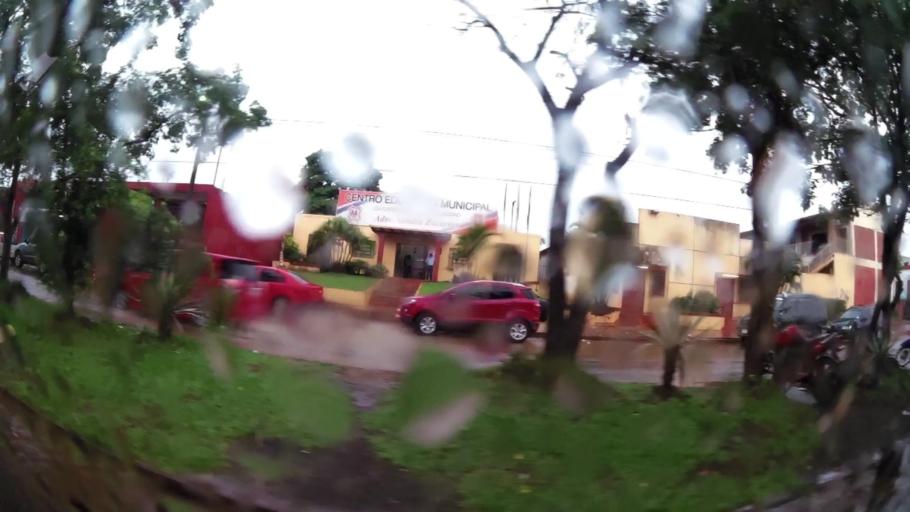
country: PY
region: Alto Parana
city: Presidente Franco
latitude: -25.5086
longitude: -54.6706
